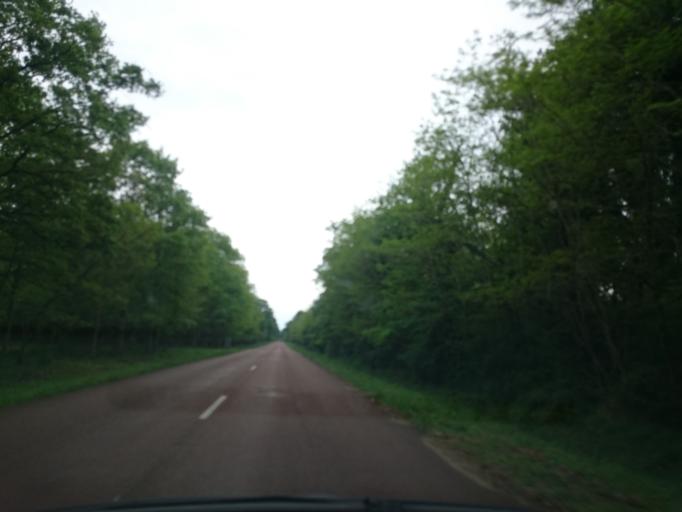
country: FR
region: Centre
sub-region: Departement du Loir-et-Cher
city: Muides-sur-Loire
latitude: 47.6449
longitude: 1.5255
